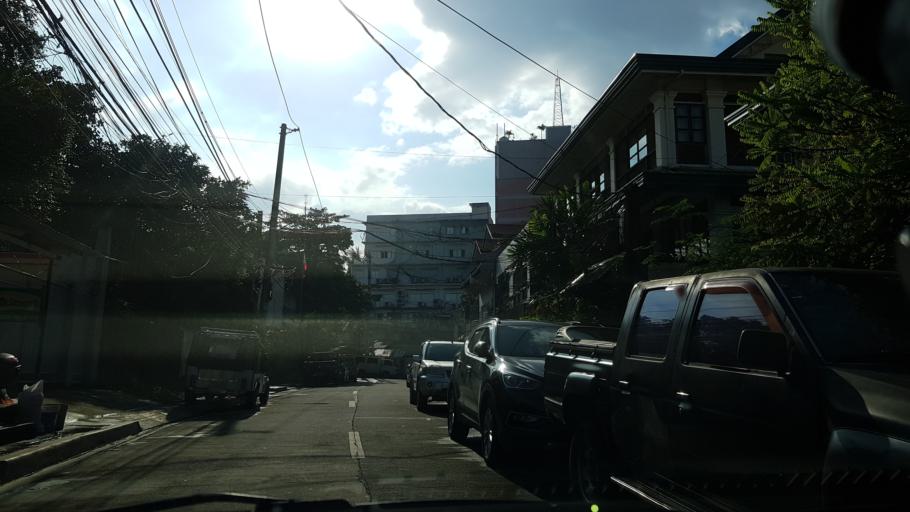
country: PH
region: Metro Manila
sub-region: Quezon City
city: Quezon City
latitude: 14.6427
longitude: 121.0507
